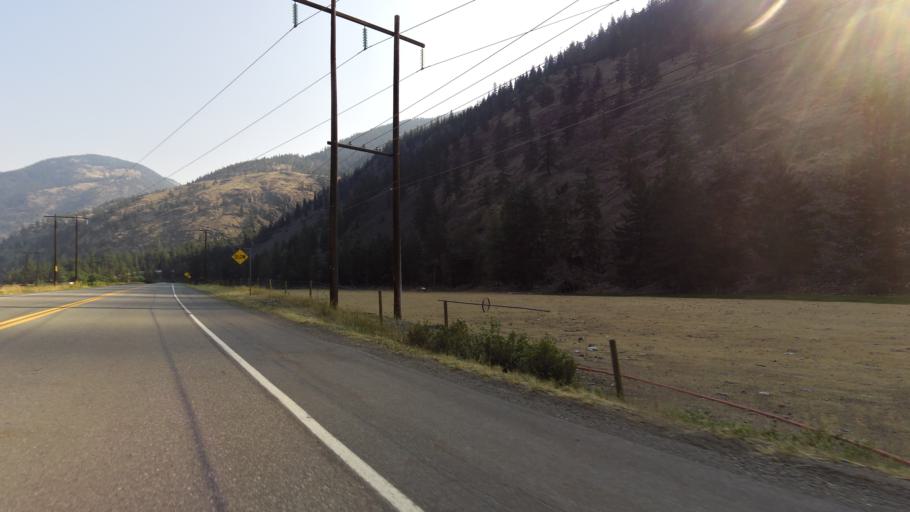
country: CA
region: British Columbia
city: Summerland
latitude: 49.2881
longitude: -120.0282
